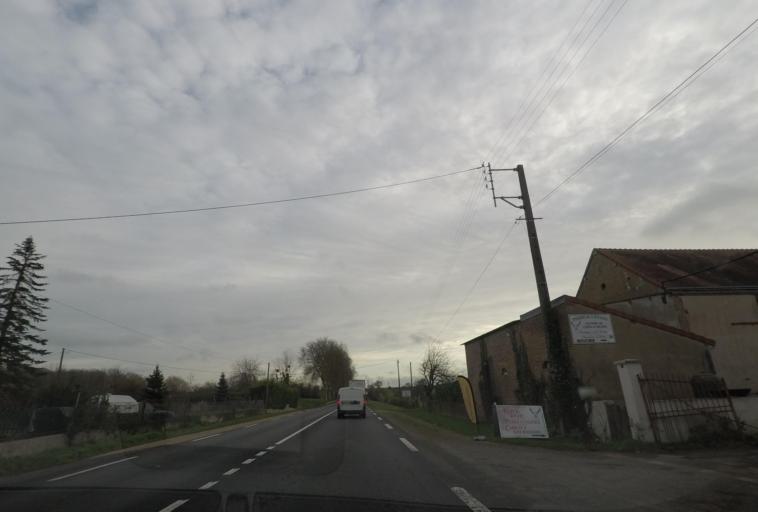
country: FR
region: Centre
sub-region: Departement du Loir-et-Cher
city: Sarge-sur-Braye
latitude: 47.9032
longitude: 0.9040
